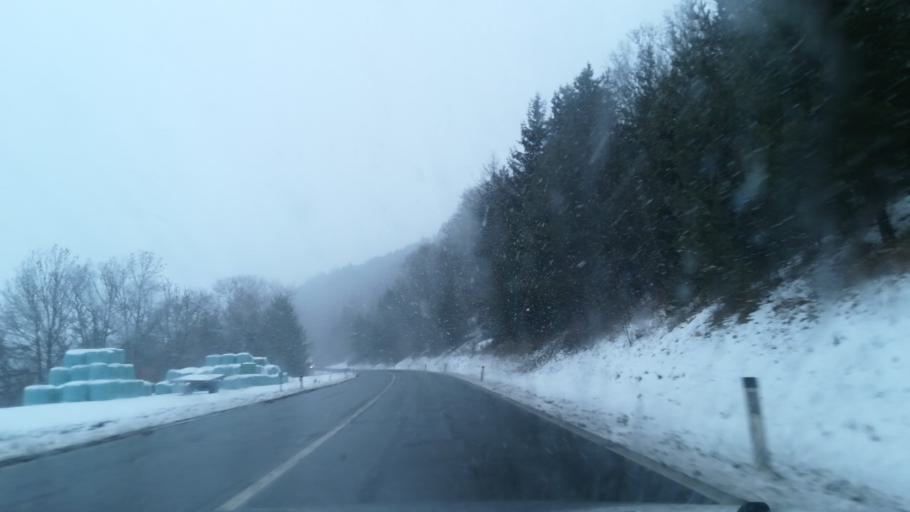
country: AT
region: Styria
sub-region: Politischer Bezirk Murtal
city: Poels
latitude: 47.2042
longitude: 14.5857
